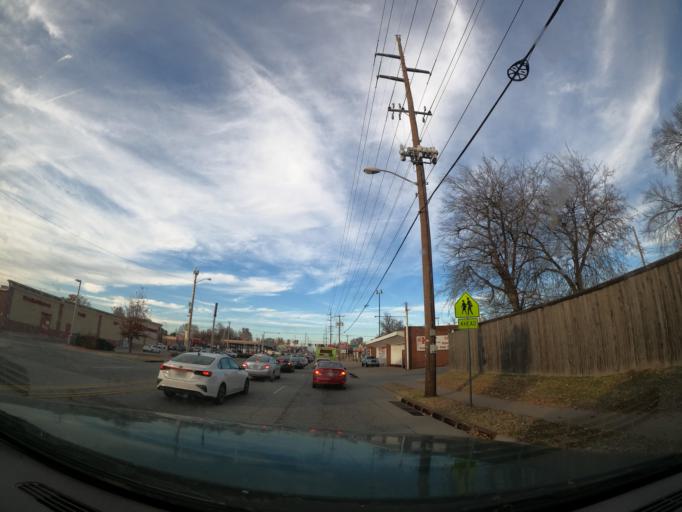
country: US
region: Oklahoma
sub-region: Tulsa County
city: Tulsa
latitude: 36.1323
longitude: -95.9403
